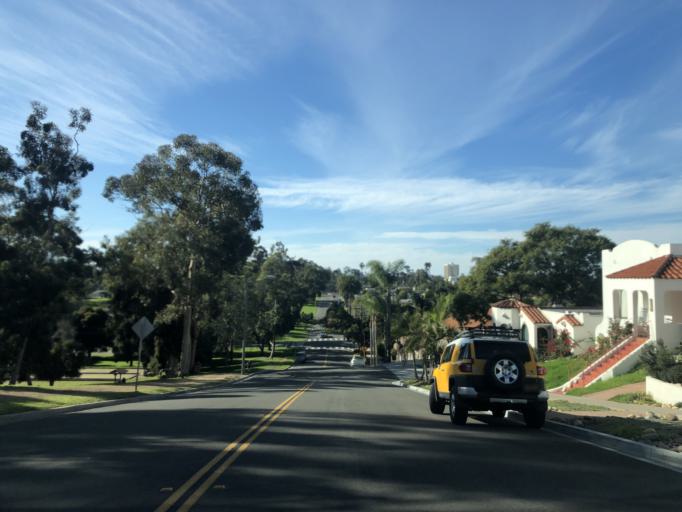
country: US
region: California
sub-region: San Diego County
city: San Diego
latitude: 32.7410
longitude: -117.1352
